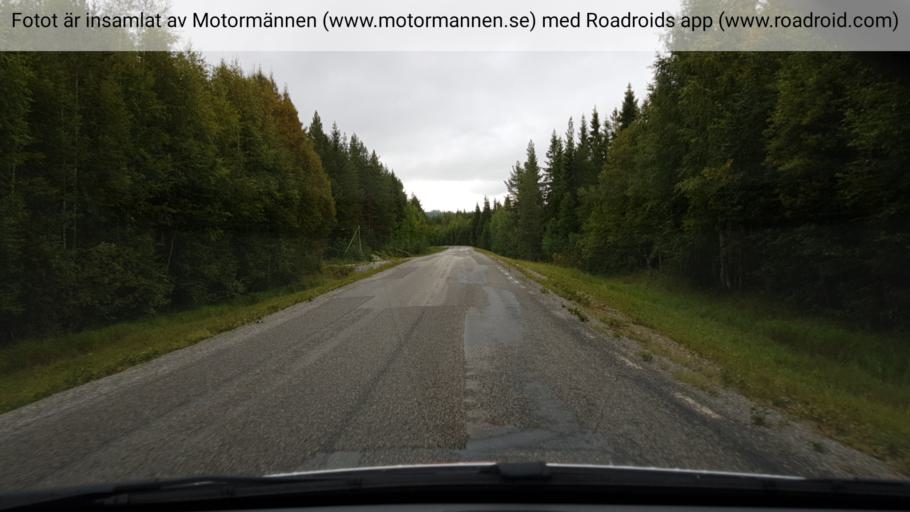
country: SE
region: Vaesterbotten
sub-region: Dorotea Kommun
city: Dorotea
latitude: 63.8236
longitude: 16.2193
